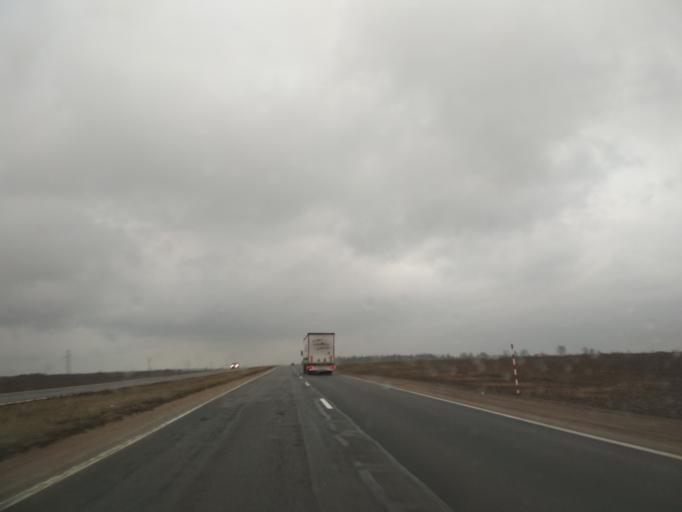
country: BY
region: Minsk
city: Dukora
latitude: 53.6419
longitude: 27.9944
